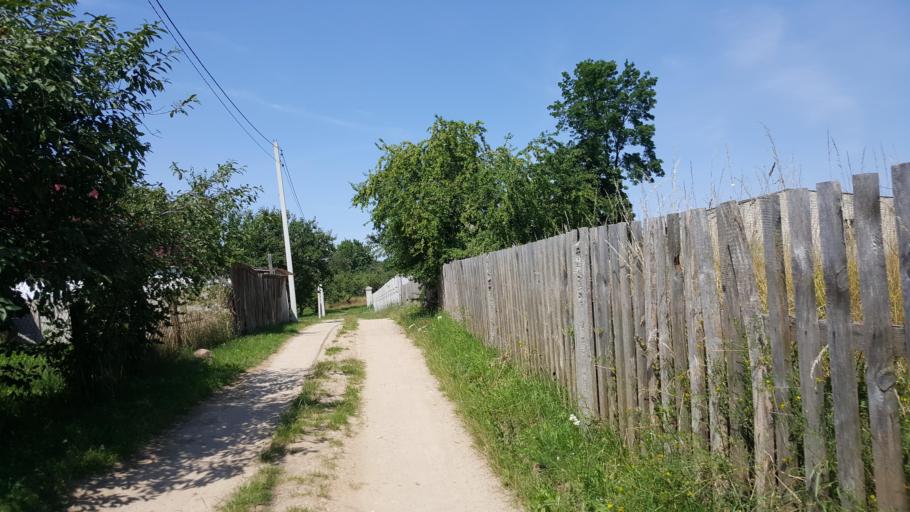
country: BY
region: Brest
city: Vysokaye
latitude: 52.3652
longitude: 23.3835
